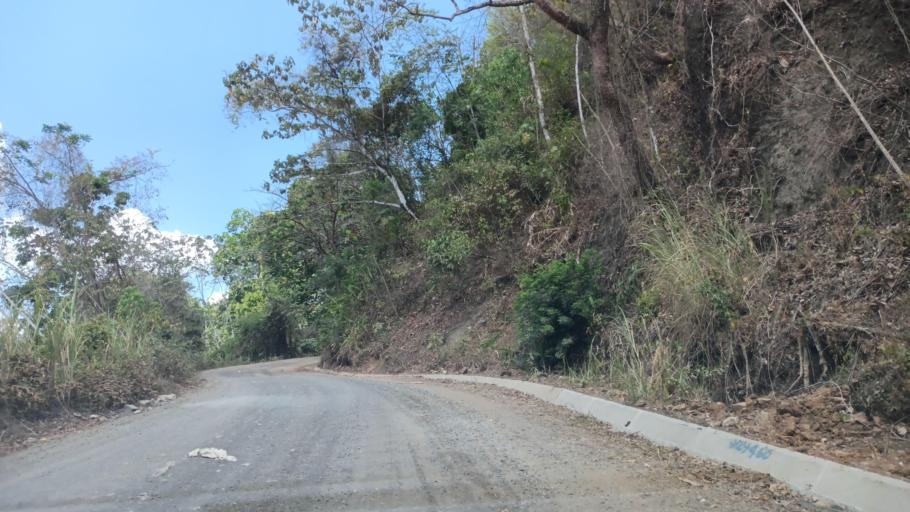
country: PA
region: Panama
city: Las Cumbres
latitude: 9.0740
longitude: -79.5735
